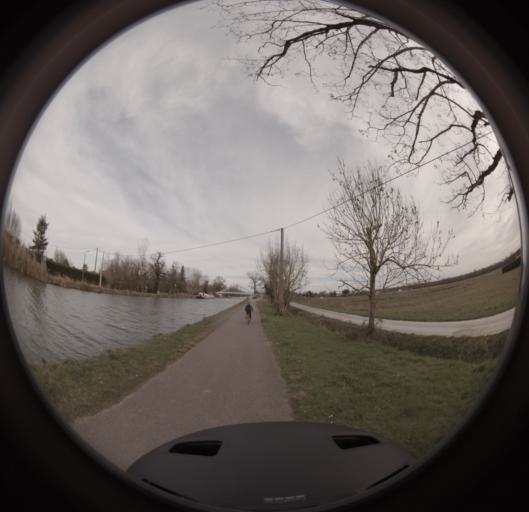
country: FR
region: Midi-Pyrenees
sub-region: Departement du Tarn-et-Garonne
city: Montech
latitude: 43.9838
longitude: 1.2621
